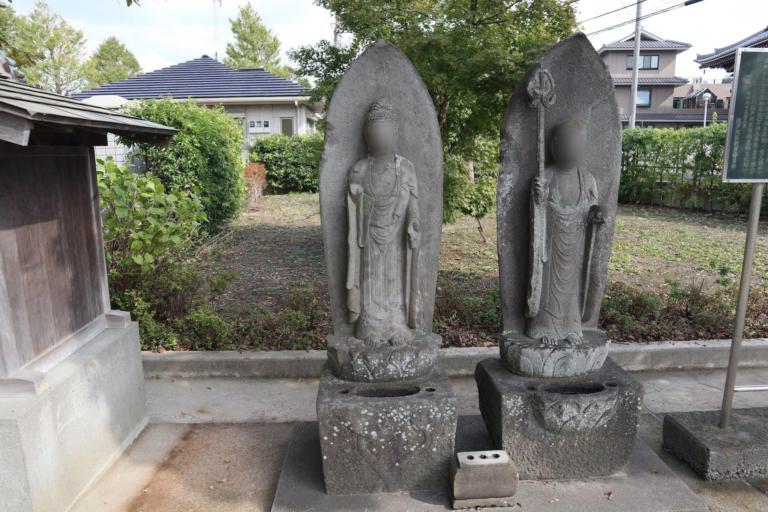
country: JP
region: Tokyo
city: Urayasu
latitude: 35.6693
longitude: 139.8816
